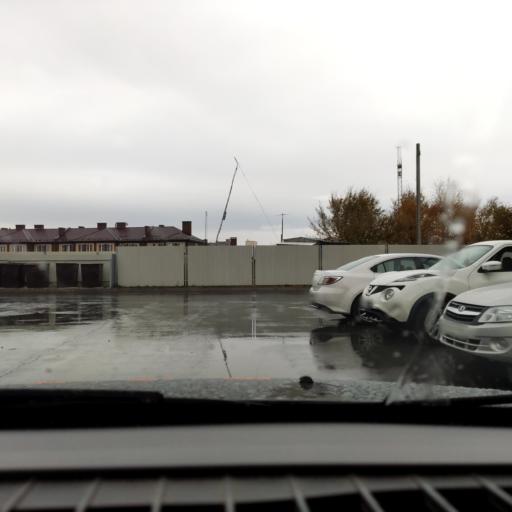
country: RU
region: Samara
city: Tol'yatti
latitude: 53.5060
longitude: 49.2486
